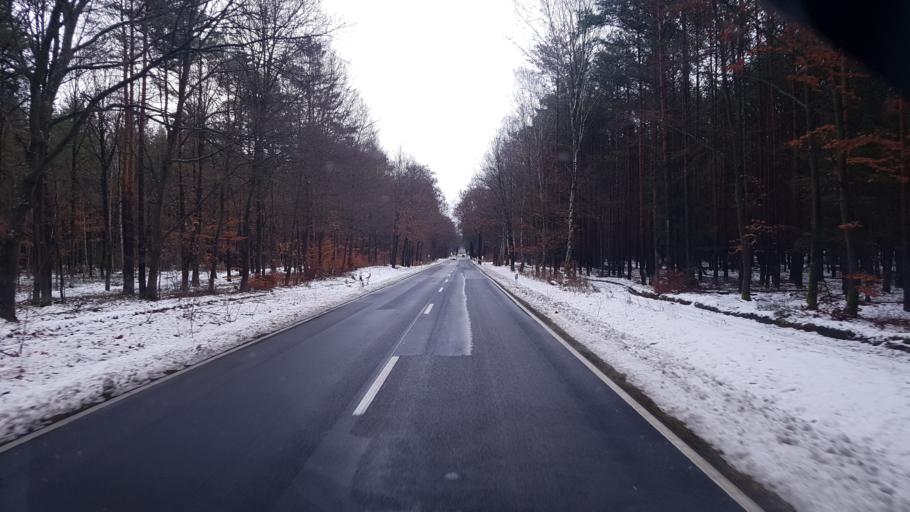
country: DE
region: Brandenburg
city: Tauer
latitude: 51.9784
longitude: 14.5025
